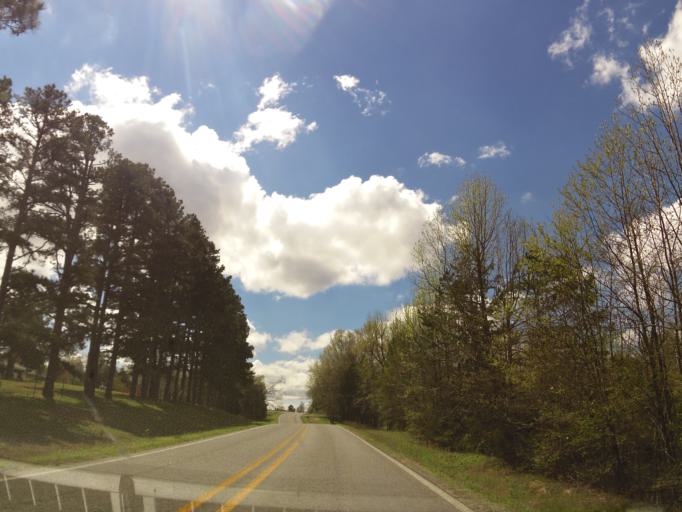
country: US
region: Arkansas
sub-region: Craighead County
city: Brookland
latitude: 36.0257
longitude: -90.6835
